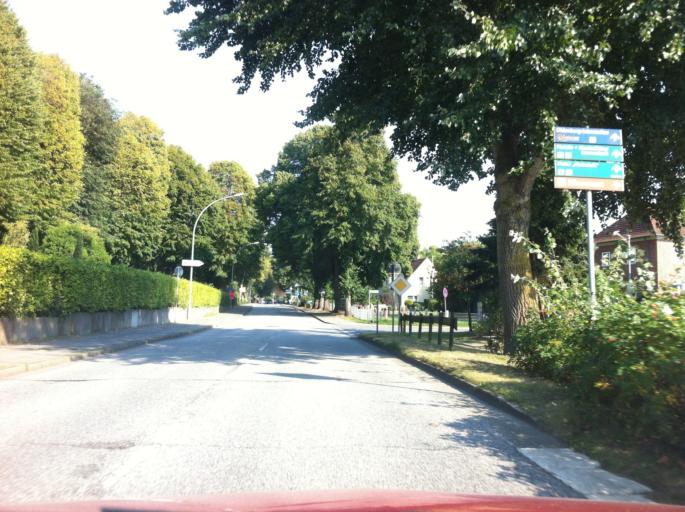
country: DE
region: Schleswig-Holstein
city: Oldenburg in Holstein
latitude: 54.2944
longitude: 10.8734
